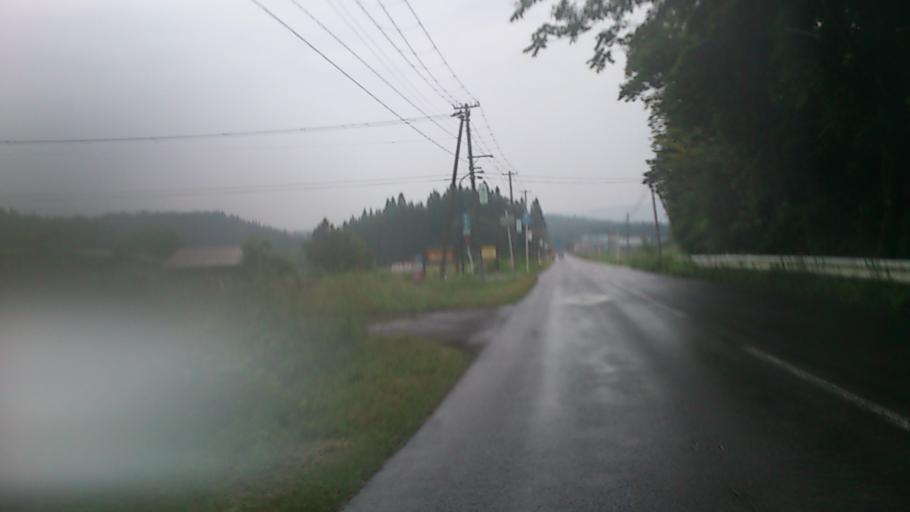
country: JP
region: Akita
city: Takanosu
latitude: 40.2490
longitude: 140.2511
